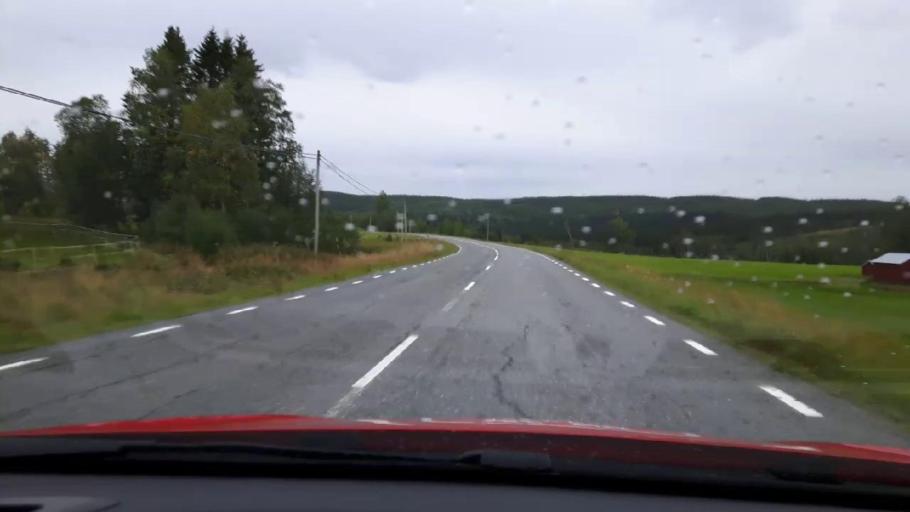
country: SE
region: Jaemtland
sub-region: Are Kommun
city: Jarpen
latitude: 63.4023
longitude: 13.3723
